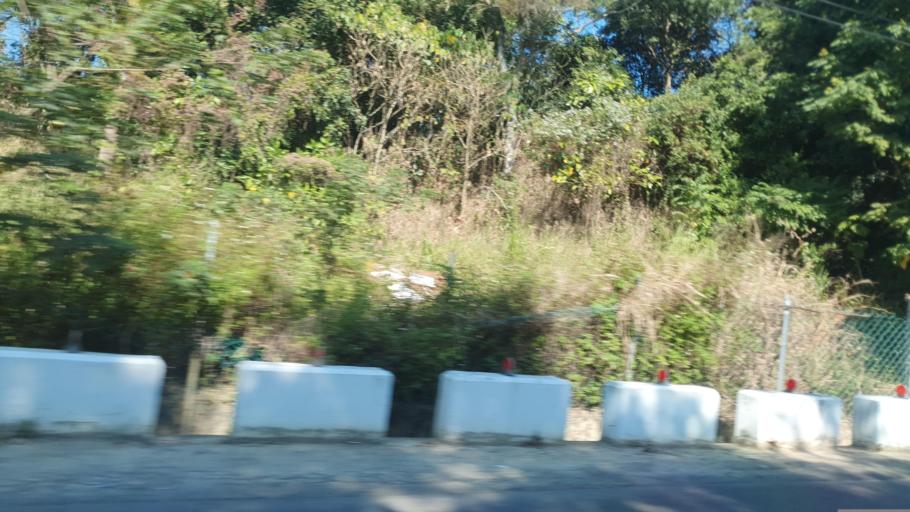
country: TW
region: Taiwan
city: Yujing
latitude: 23.0348
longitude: 120.3532
